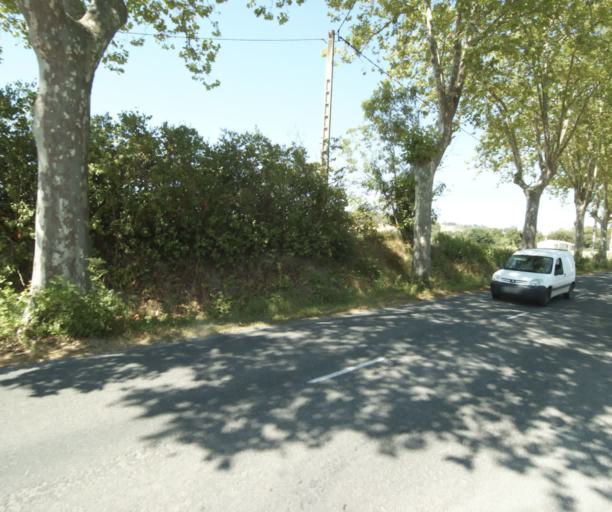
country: FR
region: Midi-Pyrenees
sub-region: Departement de la Haute-Garonne
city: Revel
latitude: 43.5021
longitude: 1.9525
